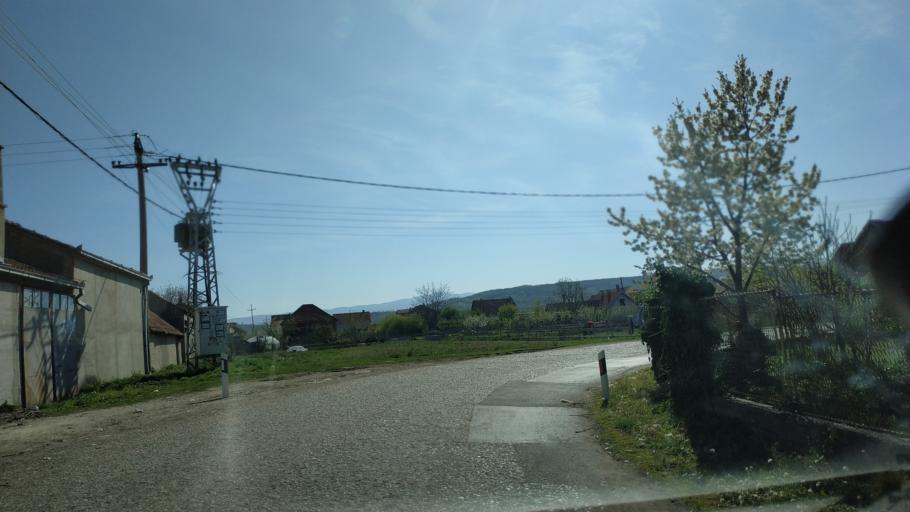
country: RS
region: Central Serbia
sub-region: Nisavski Okrug
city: Aleksinac
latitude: 43.5085
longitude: 21.6882
